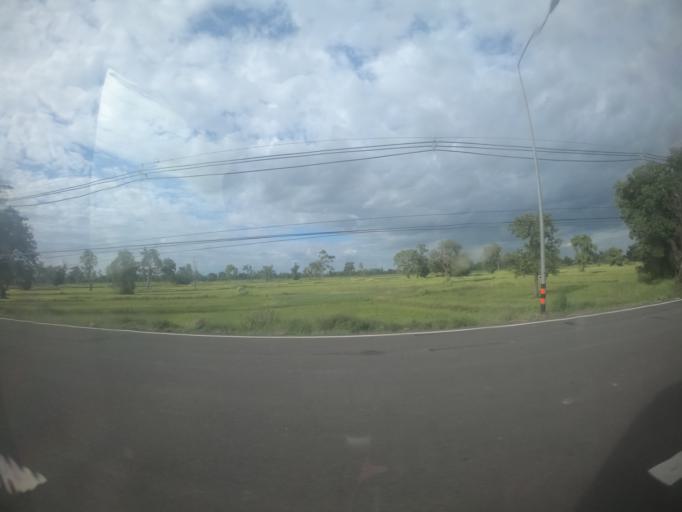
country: TH
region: Surin
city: Prasat
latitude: 14.5836
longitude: 103.4739
